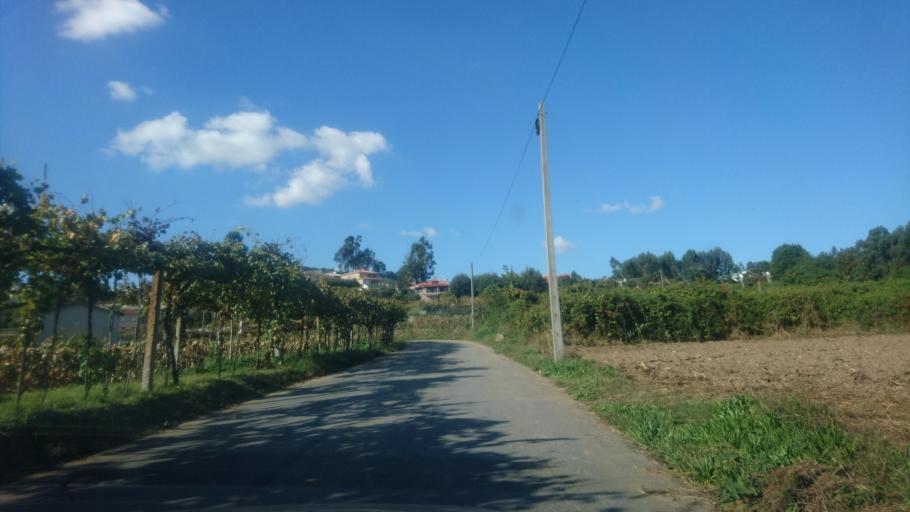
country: PT
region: Porto
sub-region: Paredes
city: Madalena
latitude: 41.2260
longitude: -8.3410
